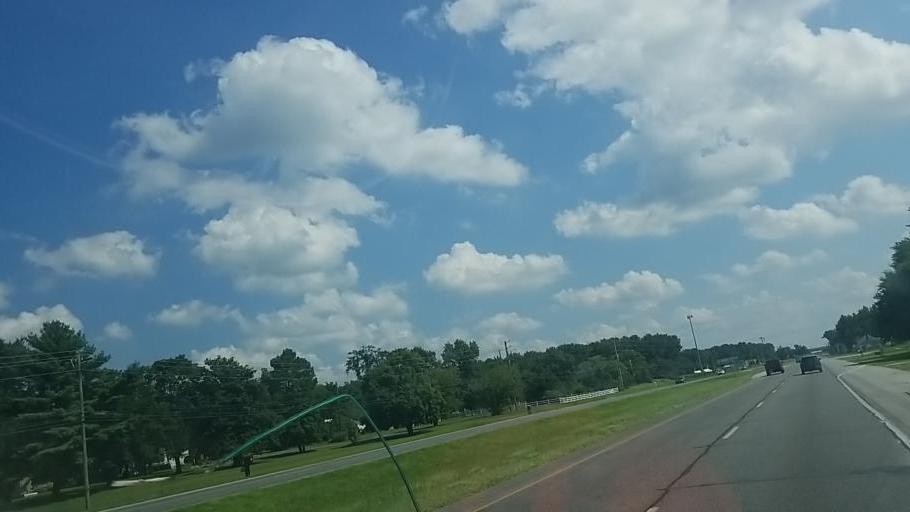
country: US
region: Delaware
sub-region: Sussex County
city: Georgetown
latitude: 38.7131
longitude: -75.4062
